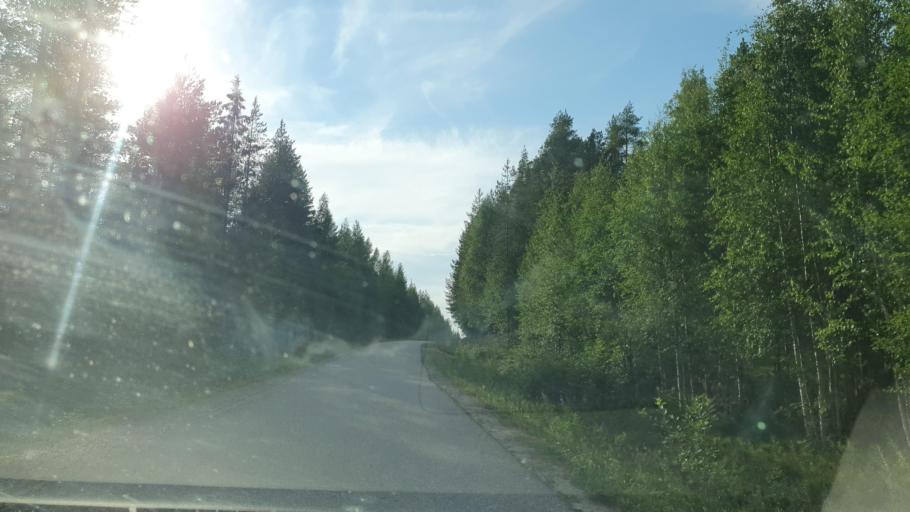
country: FI
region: Kainuu
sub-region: Kehys-Kainuu
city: Kuhmo
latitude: 64.2828
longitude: 29.3949
